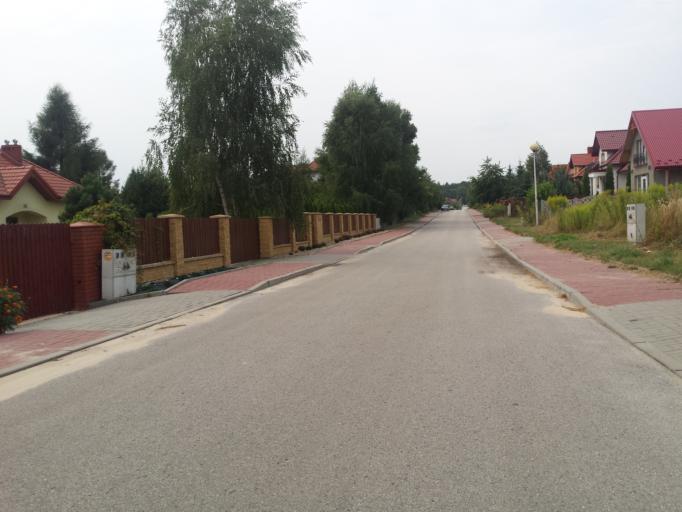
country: PL
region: Swietokrzyskie
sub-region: Powiat kielecki
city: Morawica
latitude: 50.7688
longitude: 20.6277
